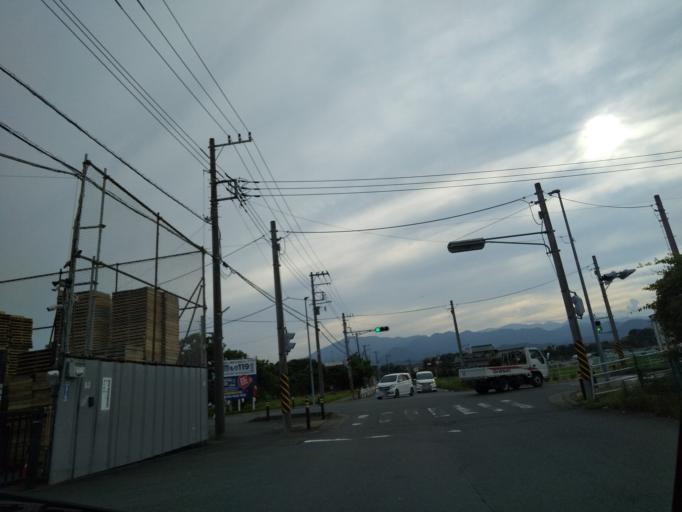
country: JP
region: Kanagawa
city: Zama
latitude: 35.4768
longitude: 139.3583
